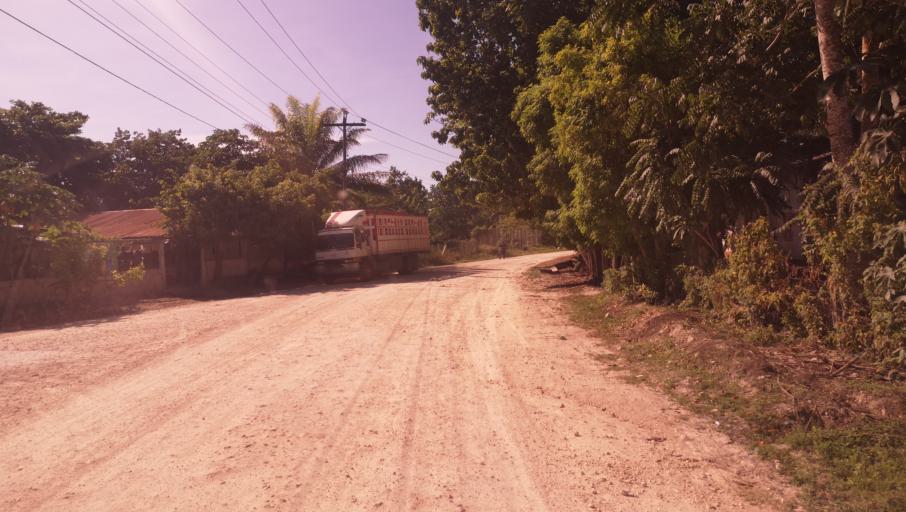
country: GT
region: Peten
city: Dolores
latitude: 16.7258
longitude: -89.3797
